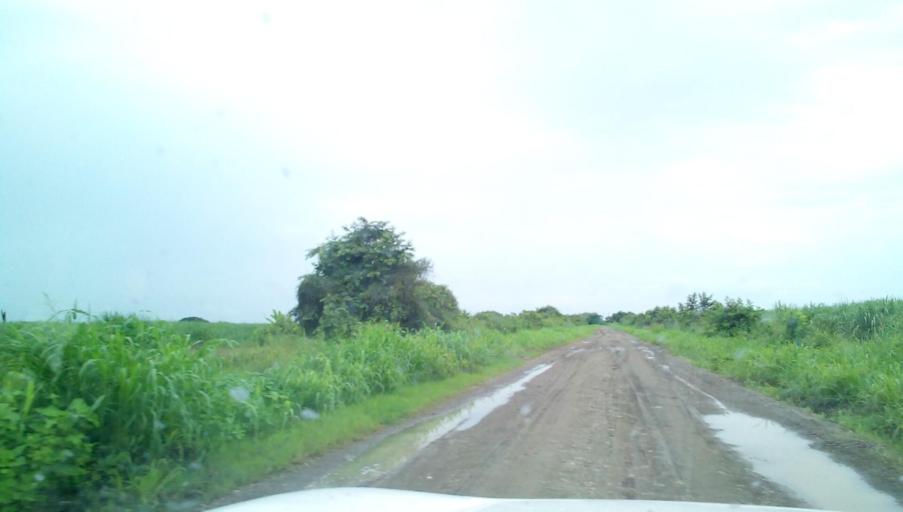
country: MX
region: Veracruz
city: Panuco
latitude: 21.8415
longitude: -98.1103
